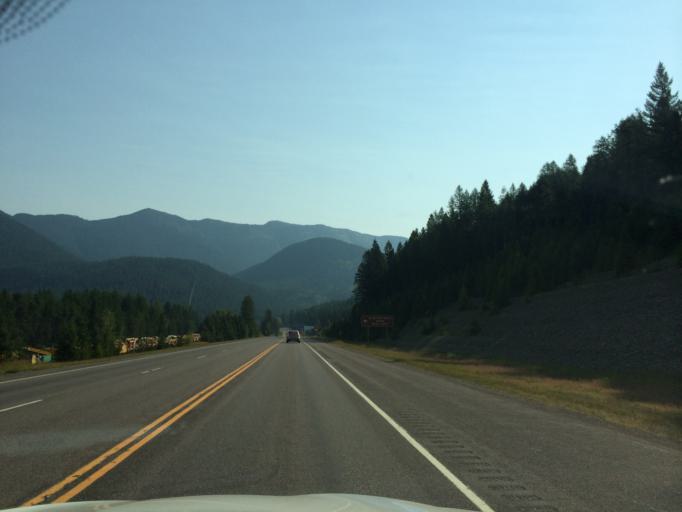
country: US
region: Montana
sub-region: Flathead County
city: Columbia Falls
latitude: 48.4914
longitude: -113.9882
